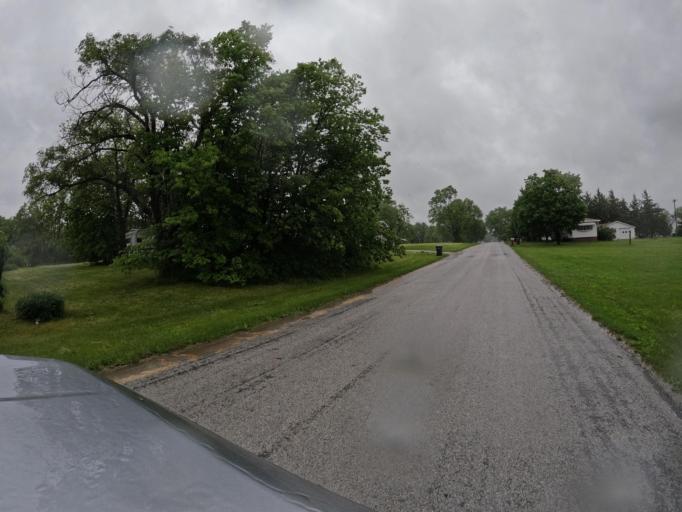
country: US
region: Nebraska
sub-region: Gage County
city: Wymore
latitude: 40.1342
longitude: -96.6599
